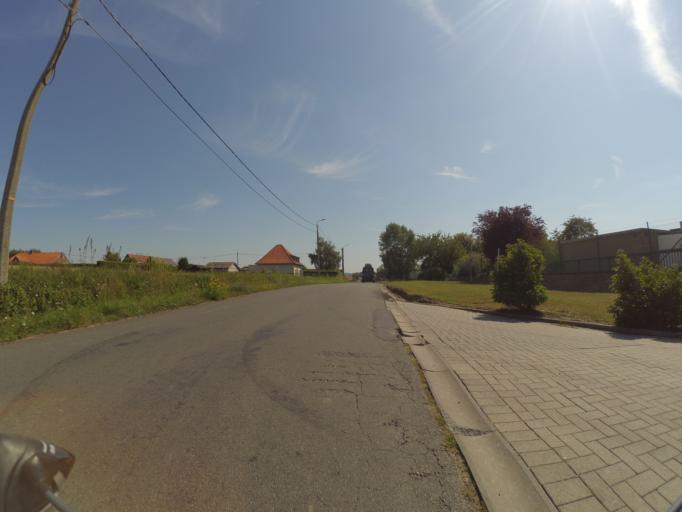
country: BE
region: Flanders
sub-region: Provincie Oost-Vlaanderen
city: Ronse
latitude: 50.7377
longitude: 3.5561
